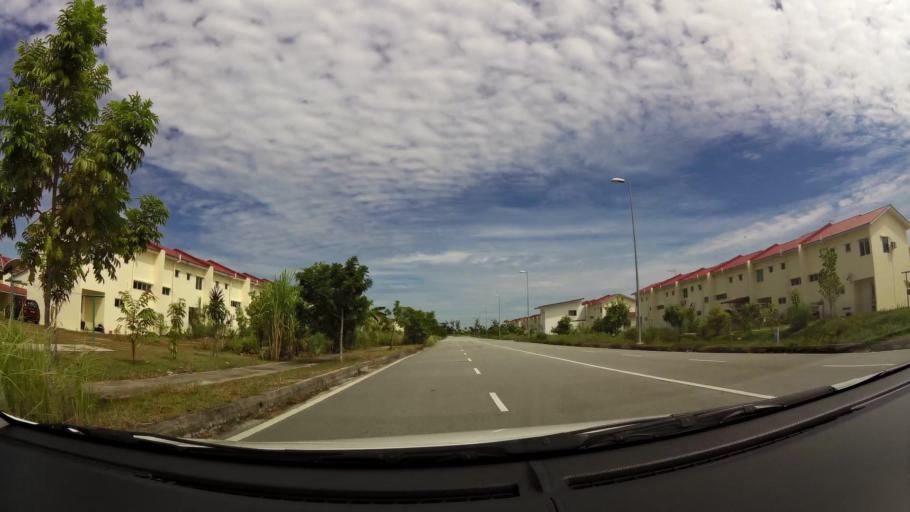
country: BN
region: Brunei and Muara
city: Bandar Seri Begawan
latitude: 4.9764
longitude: 115.0031
